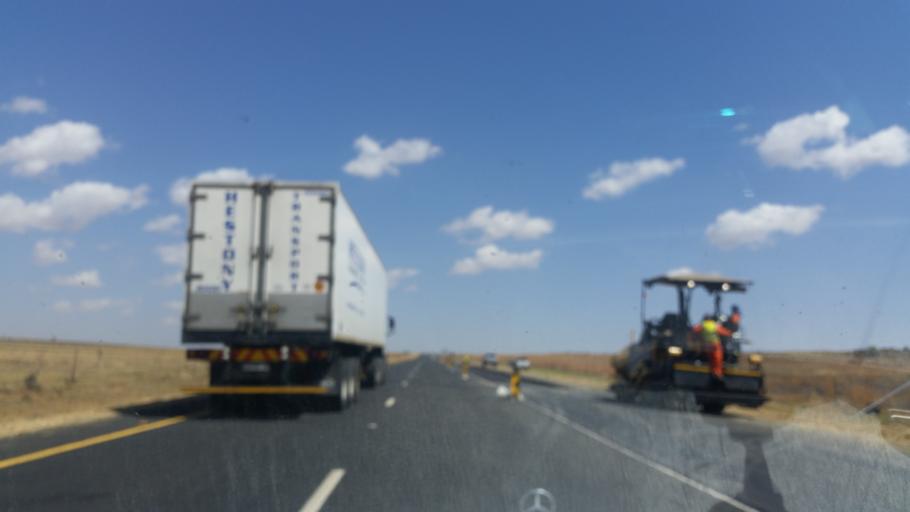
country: ZA
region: Orange Free State
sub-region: Thabo Mofutsanyana District Municipality
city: Senekal
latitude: -28.3103
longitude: 27.8443
